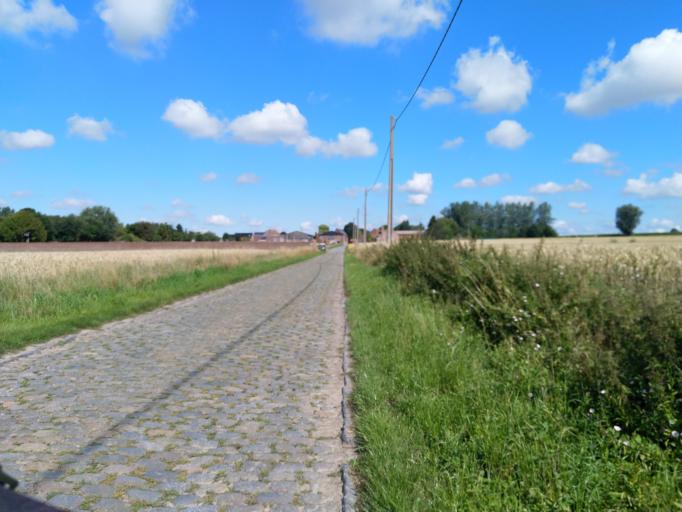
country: BE
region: Wallonia
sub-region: Province du Hainaut
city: Ath
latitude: 50.5942
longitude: 3.7604
